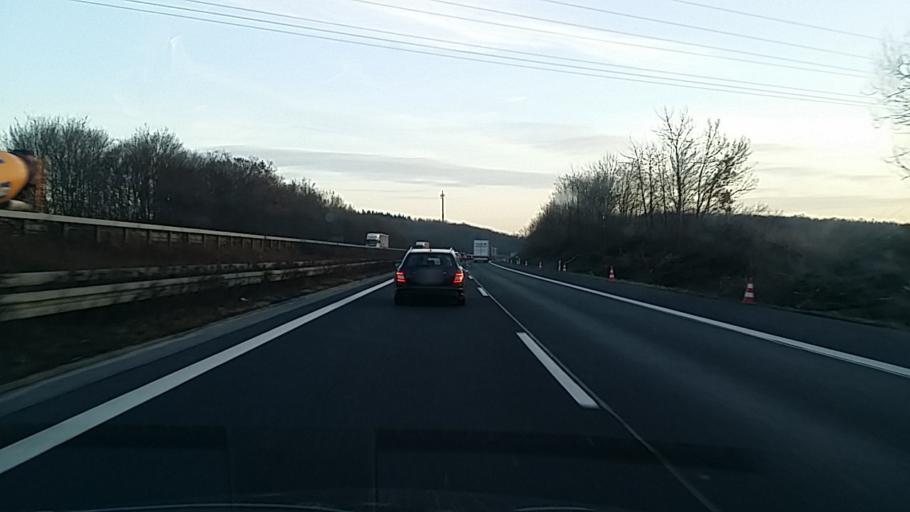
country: DE
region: Bavaria
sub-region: Regierungsbezirk Unterfranken
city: Kurnach
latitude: 49.8338
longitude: 10.0361
